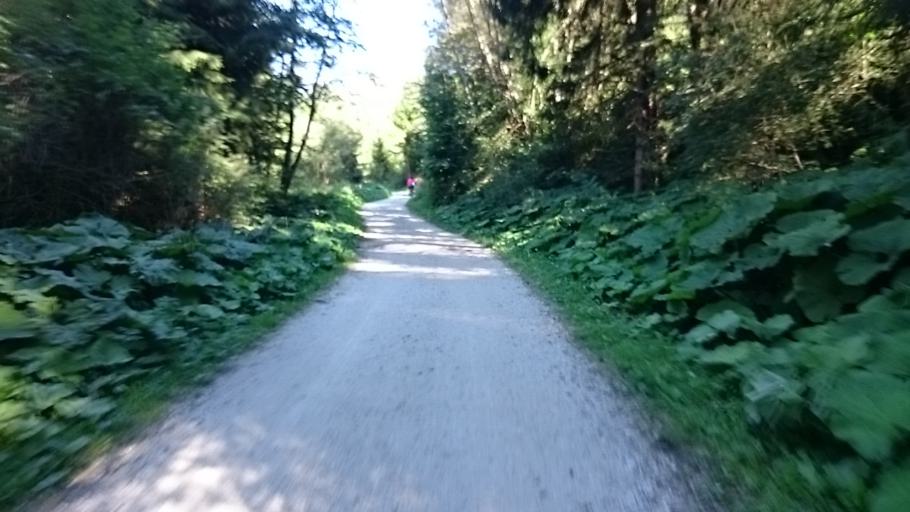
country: IT
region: Trentino-Alto Adige
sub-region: Bolzano
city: Monguelfo
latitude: 46.7607
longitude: 12.0825
